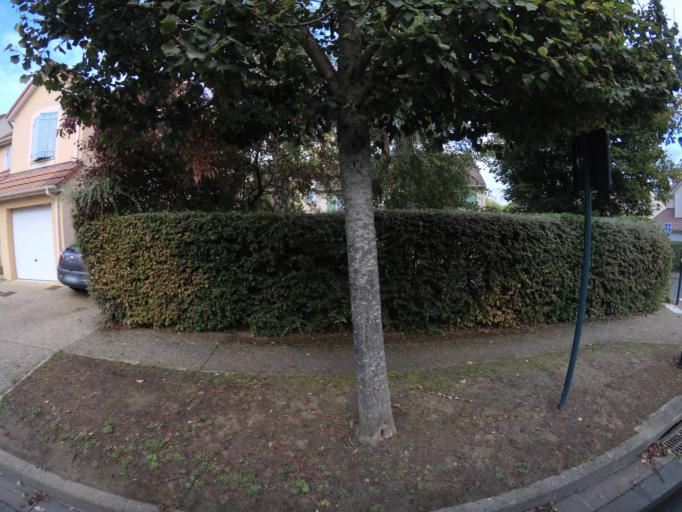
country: FR
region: Ile-de-France
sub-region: Departement de Seine-et-Marne
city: Montevrain
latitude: 48.8690
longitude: 2.7464
